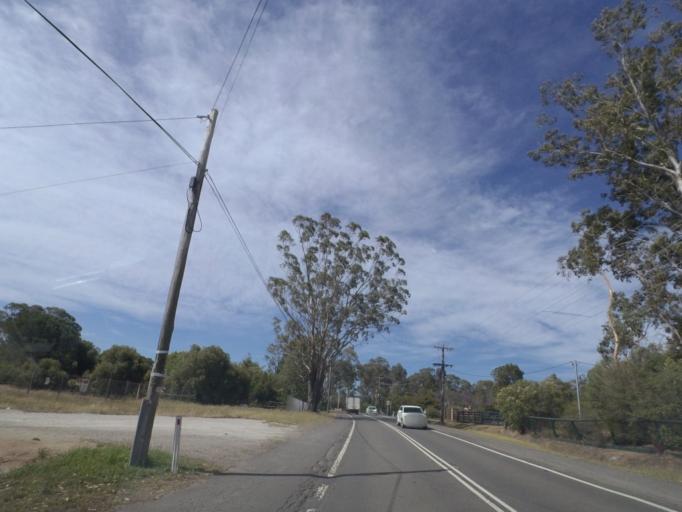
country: AU
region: New South Wales
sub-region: Campbelltown Municipality
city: Denham Court
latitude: -33.9814
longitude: 150.8482
